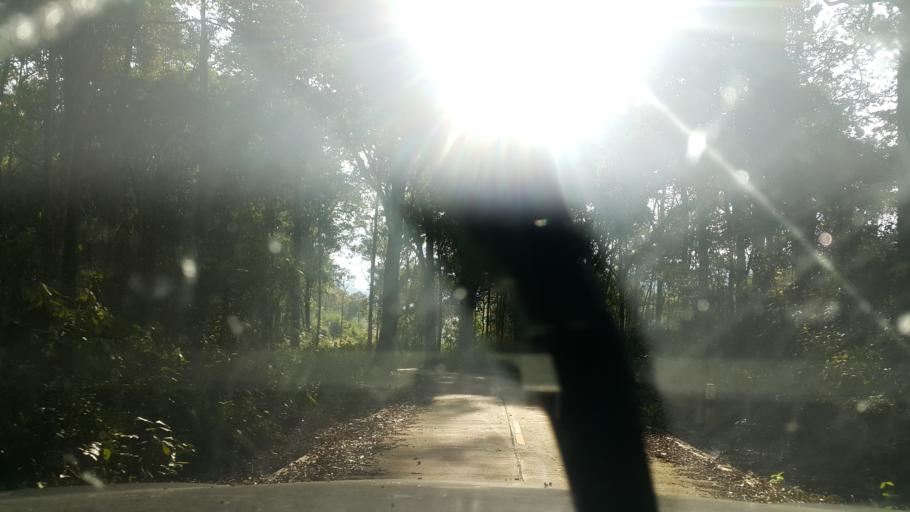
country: TH
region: Chiang Mai
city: Samoeng
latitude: 19.0063
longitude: 98.6893
